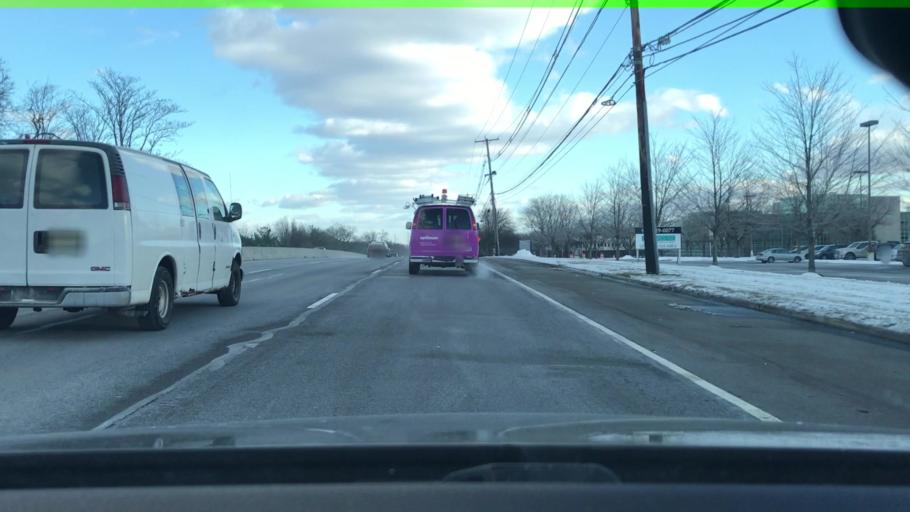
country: US
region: New Jersey
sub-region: Morris County
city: Morris Plains
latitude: 40.8416
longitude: -74.4595
